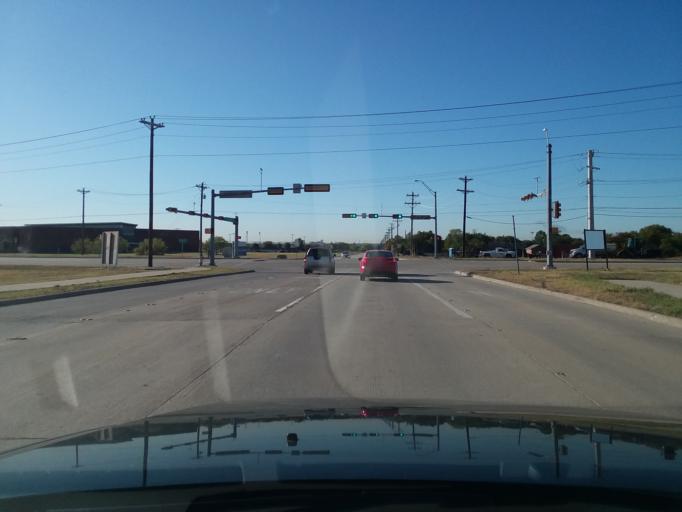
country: US
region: Texas
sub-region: Denton County
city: Lewisville
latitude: 33.0103
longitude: -97.0277
